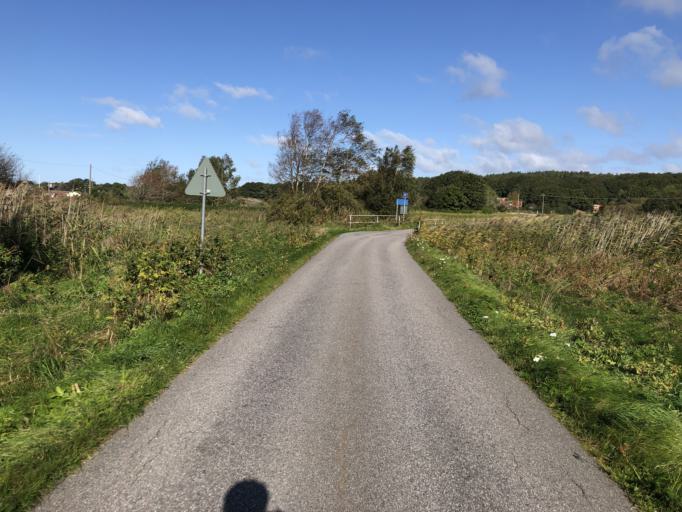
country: SE
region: Vaestra Goetaland
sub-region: Goteborg
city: Torslanda
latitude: 57.7399
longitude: 11.8192
